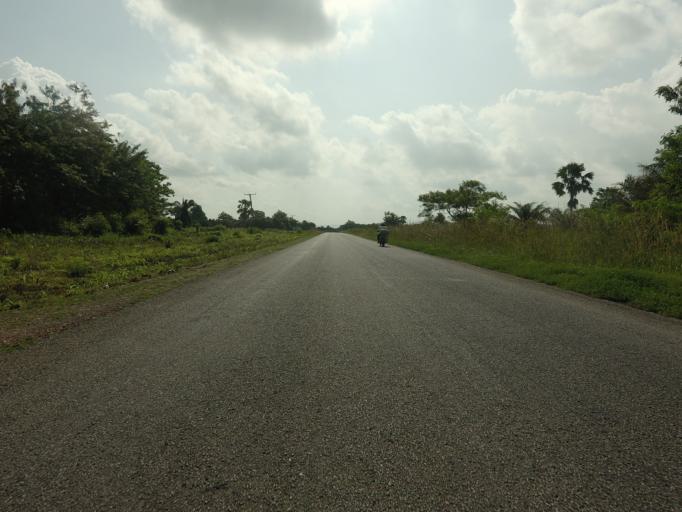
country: GH
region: Volta
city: Ho
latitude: 6.5804
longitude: 0.5793
